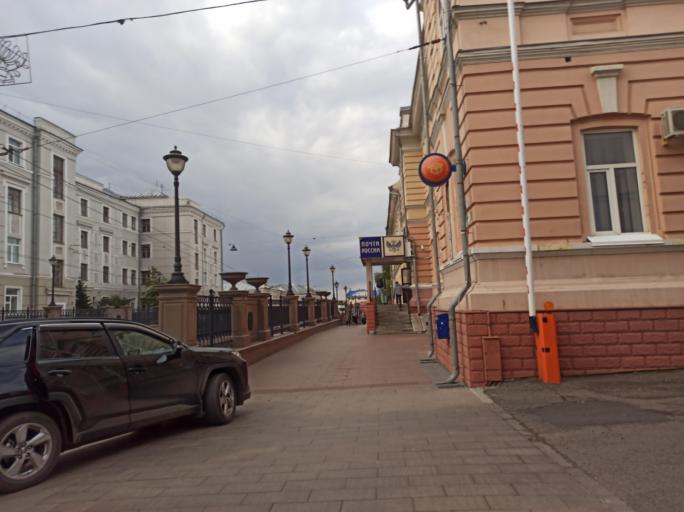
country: RU
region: Tomsk
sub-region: Tomskiy Rayon
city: Tomsk
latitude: 56.4802
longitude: 84.9499
